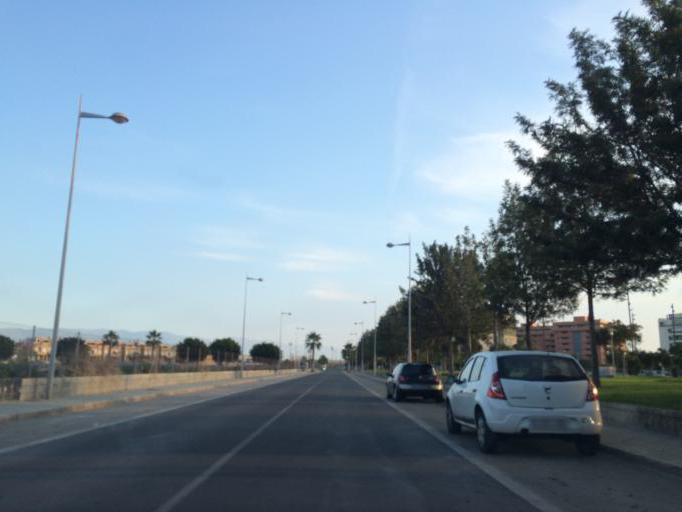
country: ES
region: Andalusia
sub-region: Provincia de Almeria
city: Almeria
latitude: 36.8332
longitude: -2.4424
